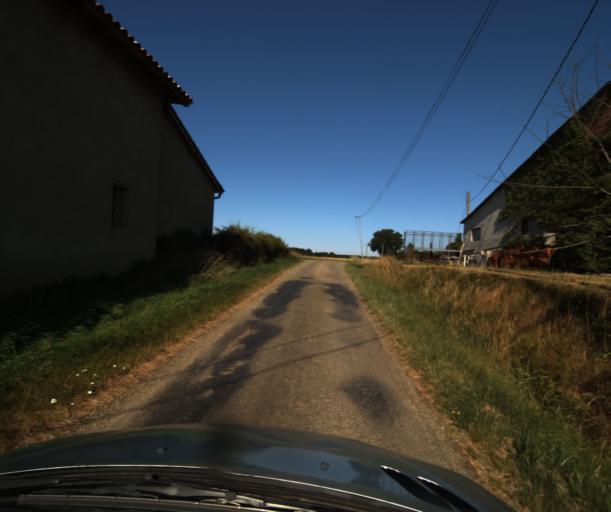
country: FR
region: Midi-Pyrenees
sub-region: Departement du Tarn-et-Garonne
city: Bressols
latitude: 43.9729
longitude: 1.3108
